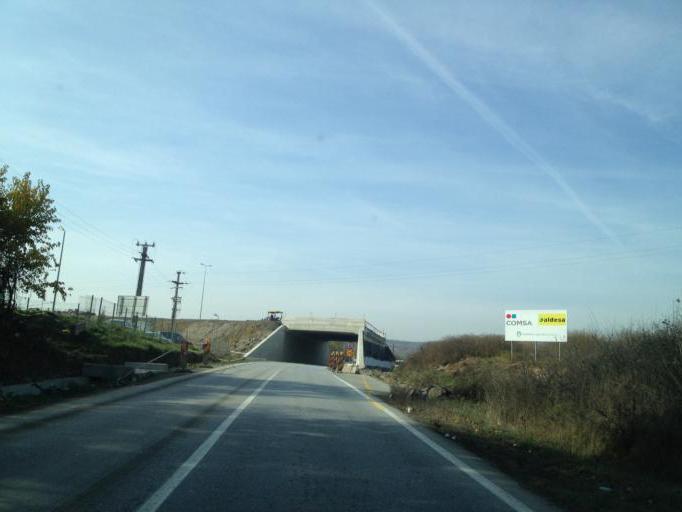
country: RO
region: Hunedoara
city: Lapugiu de Jos
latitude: 45.9130
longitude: 22.5165
